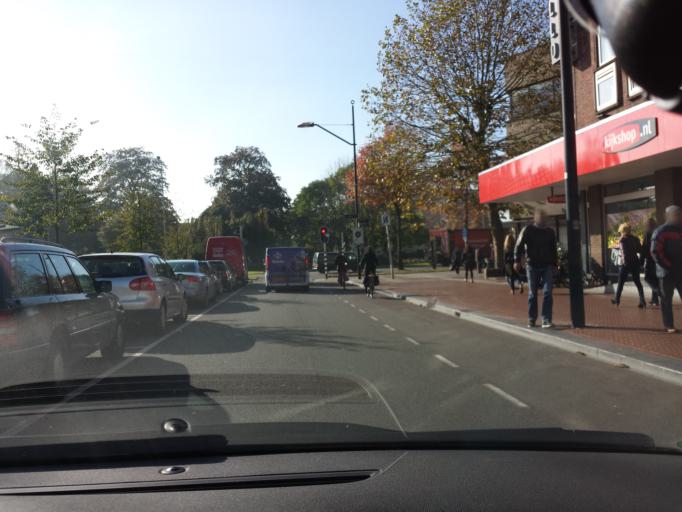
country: NL
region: Gelderland
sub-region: Gemeente Nijmegen
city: Nijmegen
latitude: 51.8430
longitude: 5.8603
